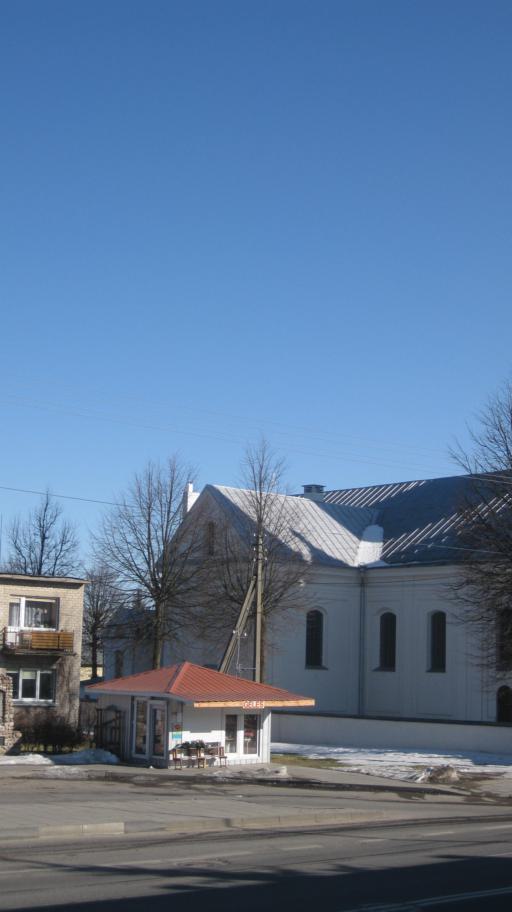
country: LT
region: Kauno apskritis
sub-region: Kauno rajonas
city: Garliava
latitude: 54.8221
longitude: 23.8730
